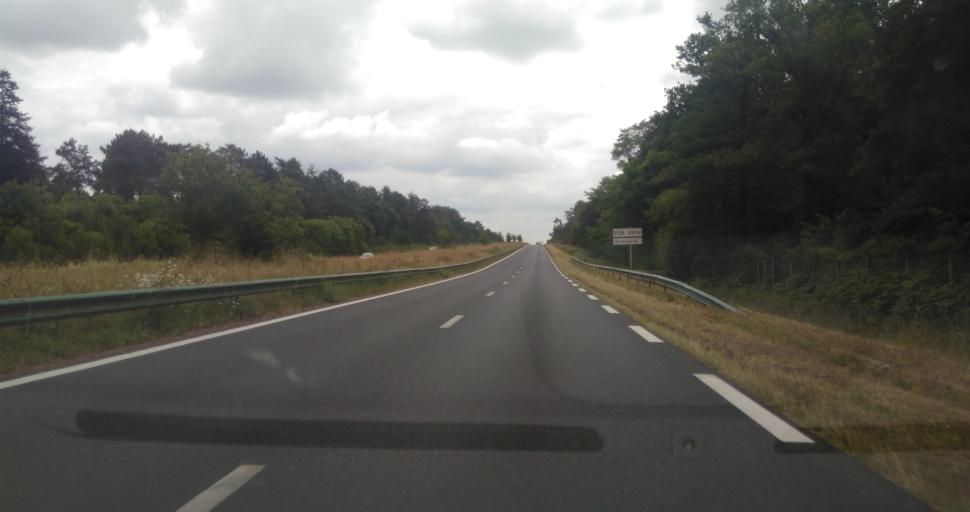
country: FR
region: Pays de la Loire
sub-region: Departement de la Vendee
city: Bournezeau
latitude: 46.6492
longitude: -1.2174
